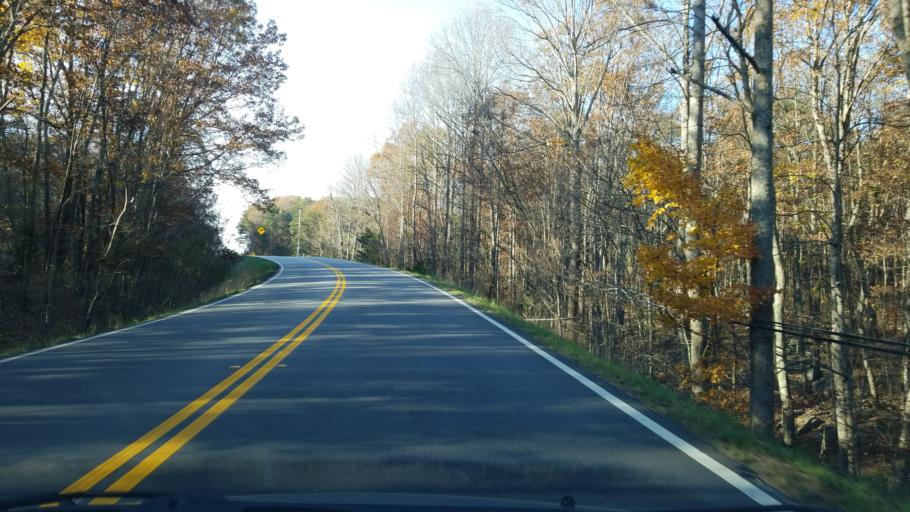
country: US
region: Georgia
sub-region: Dade County
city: Trenton
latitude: 34.8238
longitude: -85.5006
